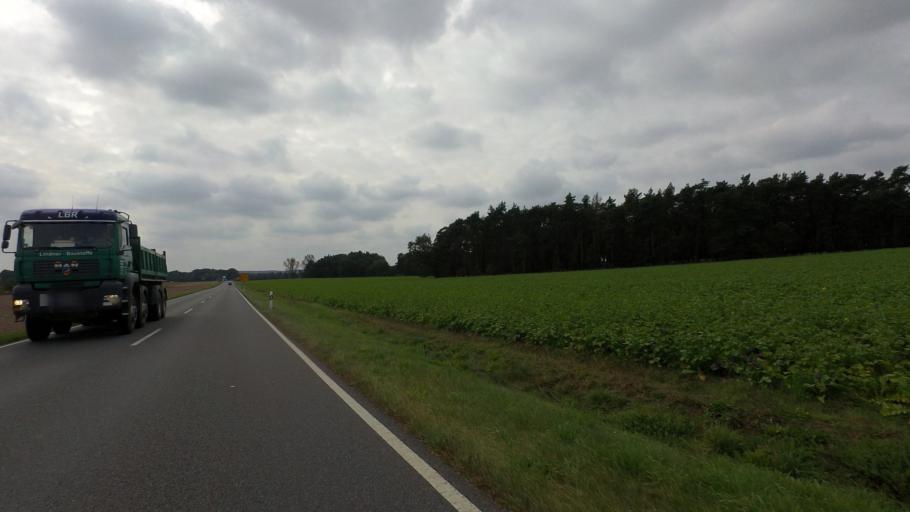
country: DE
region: Brandenburg
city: Luckau
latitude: 51.8201
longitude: 13.6801
